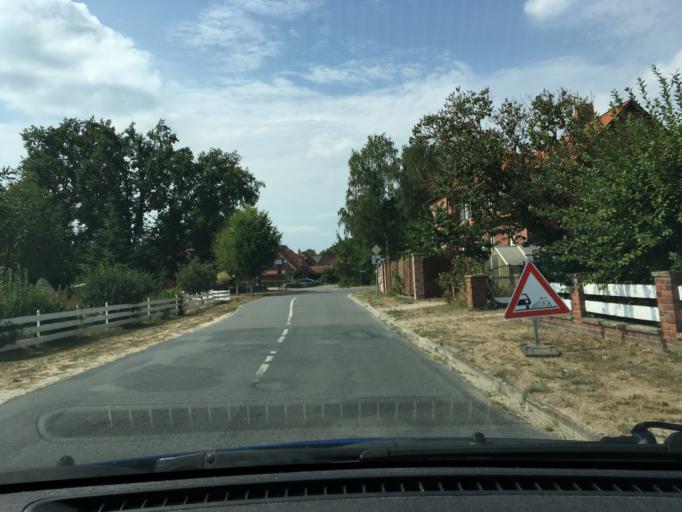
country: DE
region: Lower Saxony
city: Barnstedt
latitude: 53.1239
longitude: 10.4253
